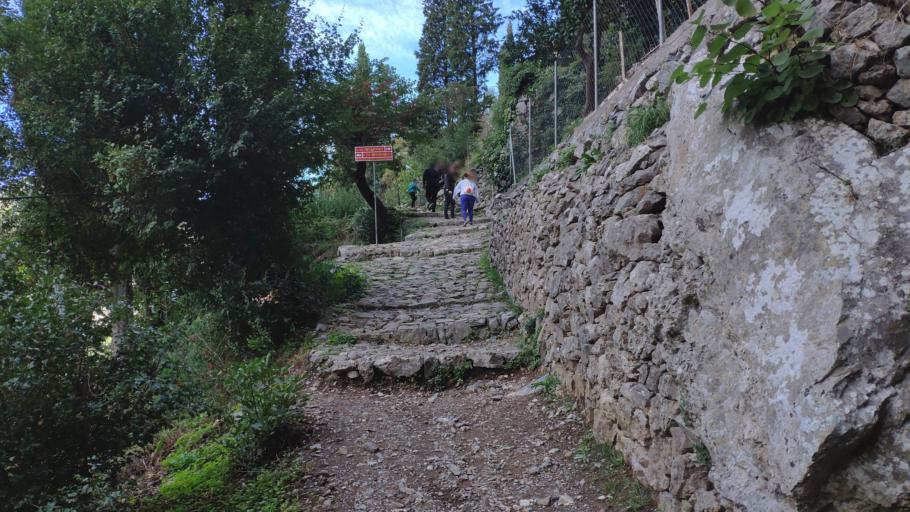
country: GR
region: Peloponnese
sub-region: Nomos Arkadias
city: Dimitsana
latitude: 37.5479
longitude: 22.0534
